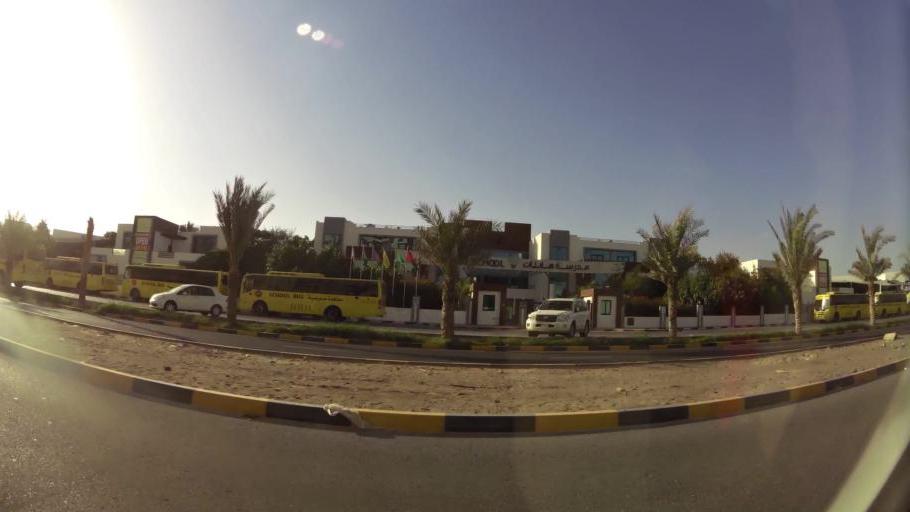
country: AE
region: Ajman
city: Ajman
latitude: 25.3995
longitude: 55.4854
